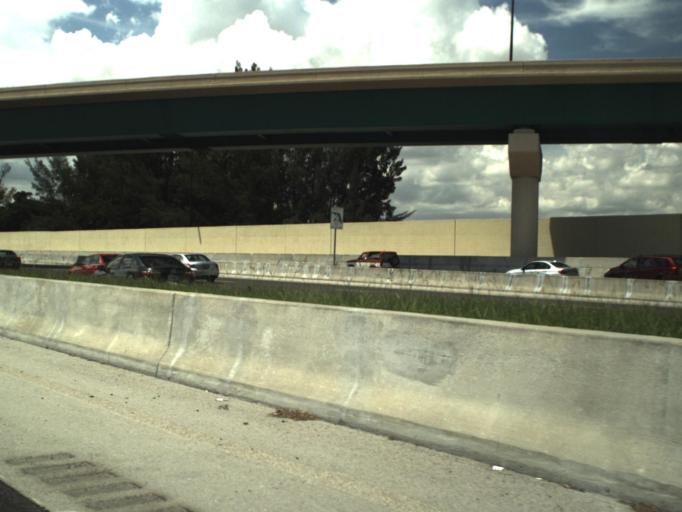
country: US
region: Florida
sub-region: Broward County
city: Broadview Park
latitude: 26.0914
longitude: -80.2183
